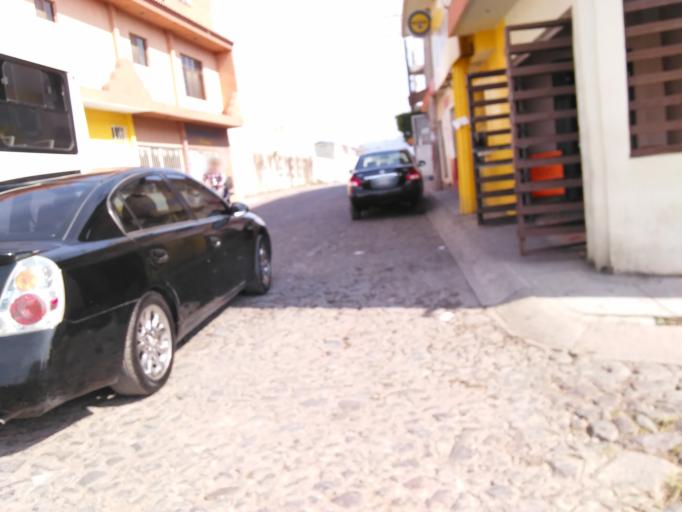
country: MX
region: Nayarit
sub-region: Tepic
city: La Corregidora
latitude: 21.4884
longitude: -104.8446
